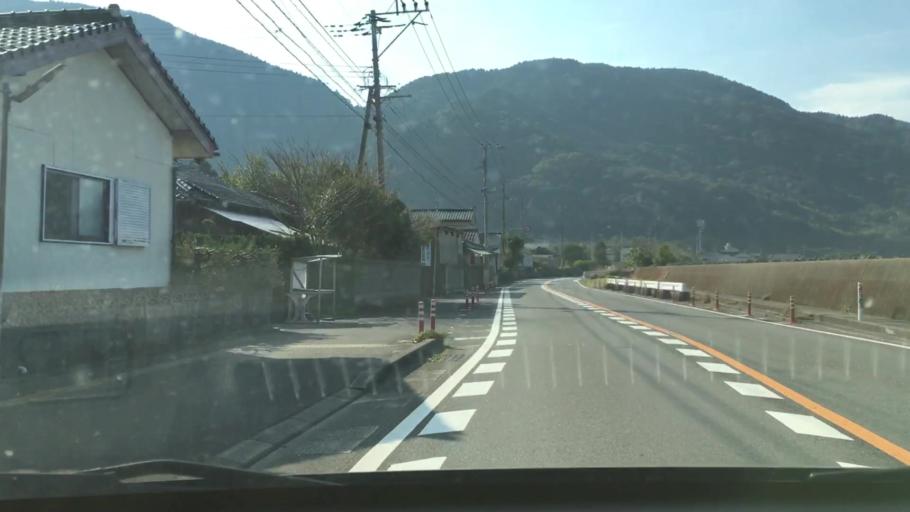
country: JP
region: Kagoshima
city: Kokubu-matsuki
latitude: 31.6517
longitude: 130.8223
